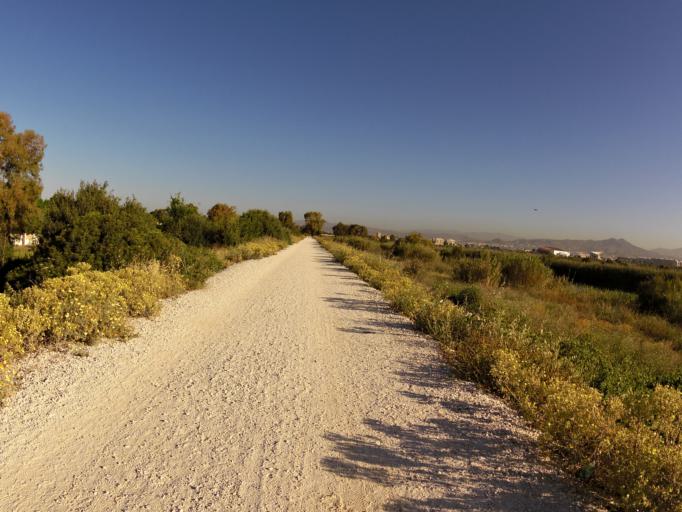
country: ES
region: Andalusia
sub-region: Provincia de Malaga
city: Torremolinos
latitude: 36.6685
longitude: -4.4584
